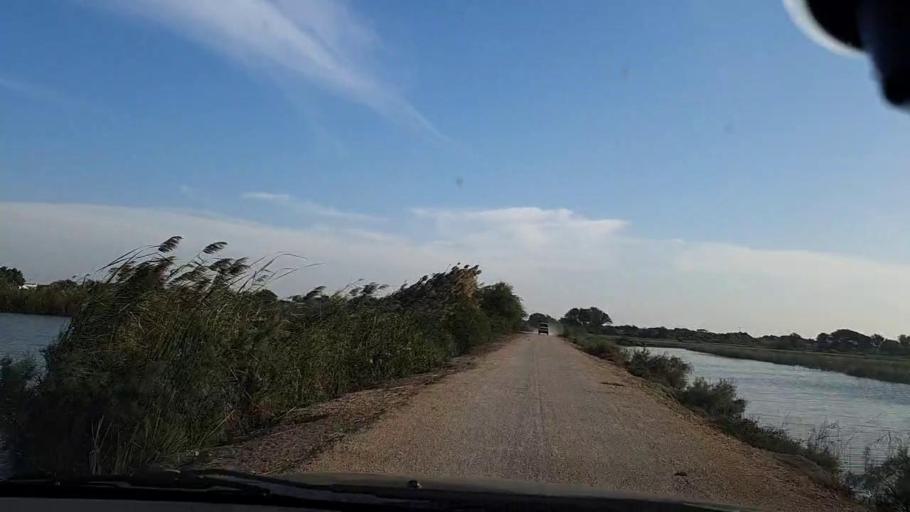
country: PK
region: Sindh
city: Mirpur Batoro
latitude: 24.6533
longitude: 68.2934
